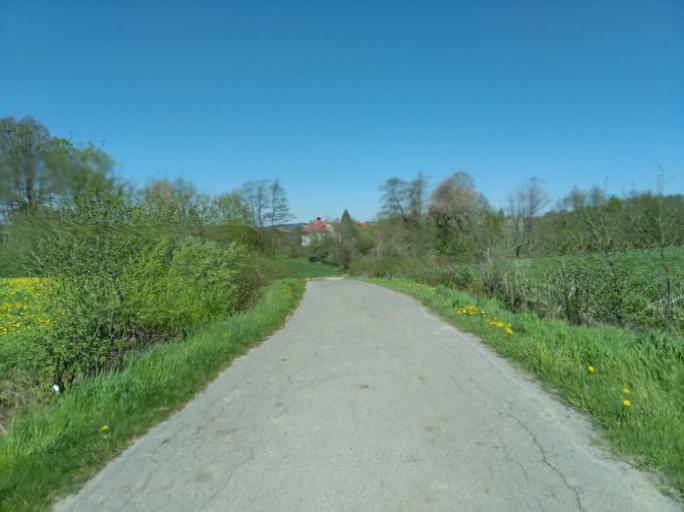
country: PL
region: Subcarpathian Voivodeship
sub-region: Powiat ropczycko-sedziszowski
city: Wielopole Skrzynskie
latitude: 49.9137
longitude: 21.5481
